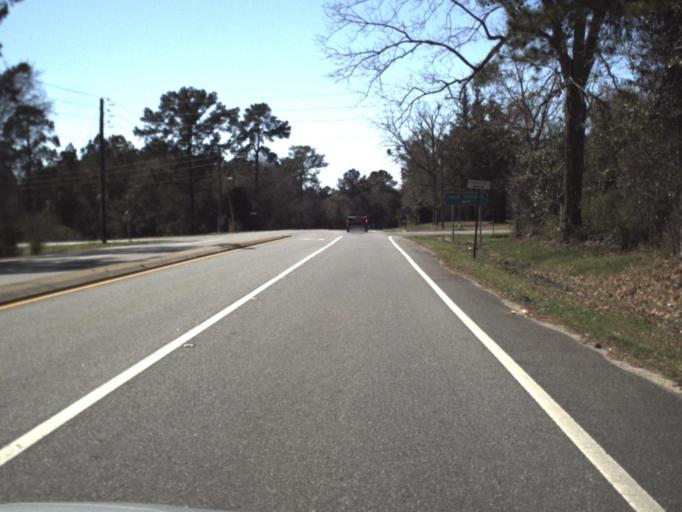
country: US
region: Florida
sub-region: Jackson County
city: Marianna
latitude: 30.7500
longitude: -85.2795
